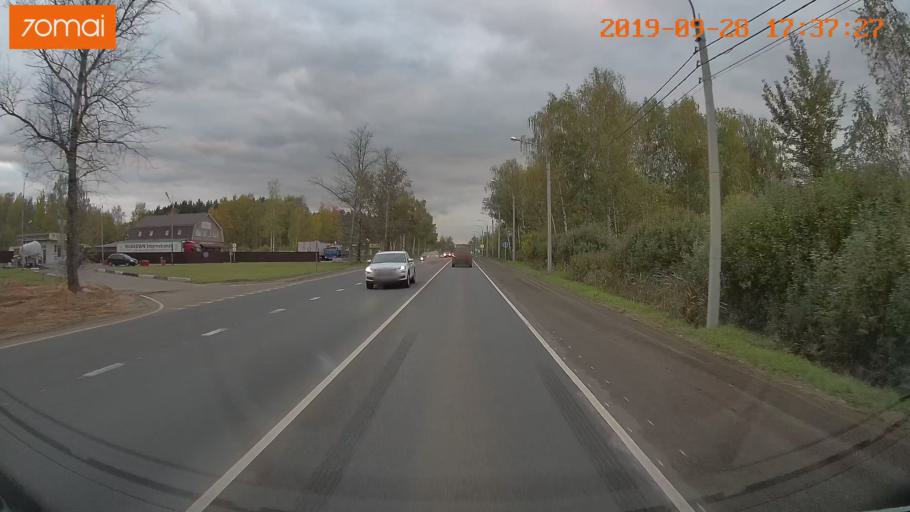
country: RU
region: Jaroslavl
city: Yaroslavl
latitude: 57.5427
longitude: 39.9505
